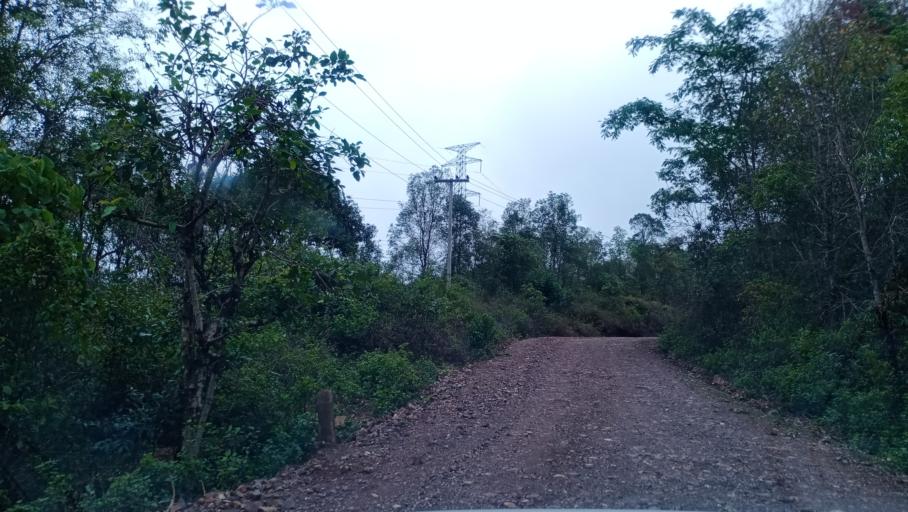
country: LA
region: Phongsali
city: Phongsali
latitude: 21.3448
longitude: 102.0902
